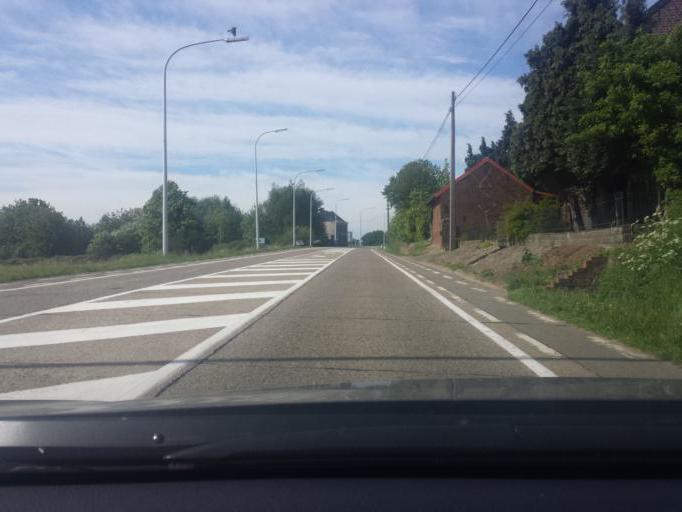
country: BE
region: Flanders
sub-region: Provincie Vlaams-Brabant
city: Diest
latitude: 50.9624
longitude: 5.0254
